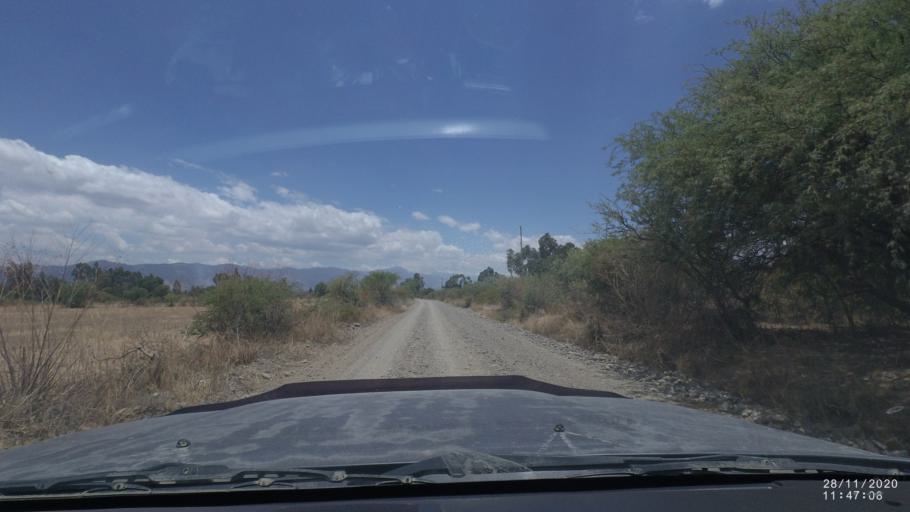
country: BO
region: Cochabamba
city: Tarata
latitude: -17.6468
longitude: -66.0383
